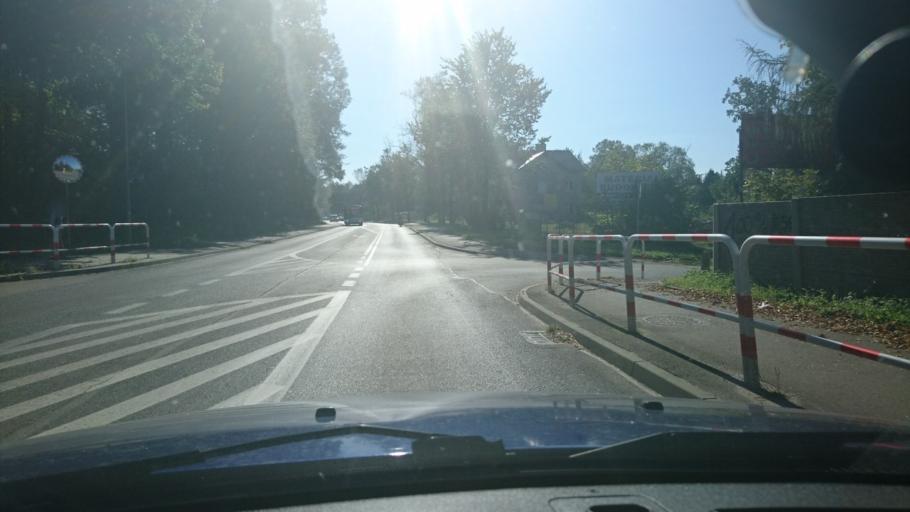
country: PL
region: Silesian Voivodeship
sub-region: Powiat bielski
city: Czechowice-Dziedzice
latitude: 49.9067
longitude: 18.9994
